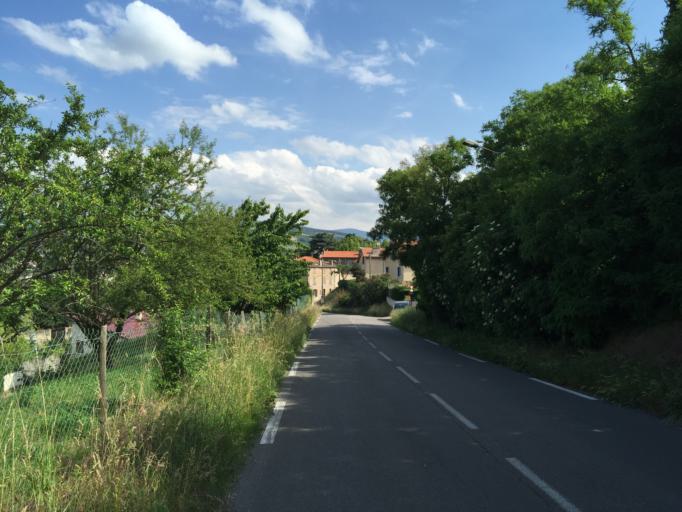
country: FR
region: Rhone-Alpes
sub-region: Departement de la Loire
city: Saint-Chamond
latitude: 45.4816
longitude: 4.5079
